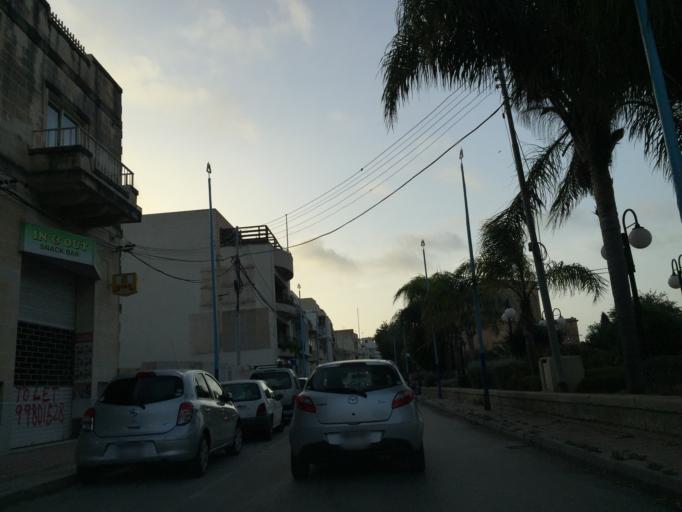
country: MT
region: Saint Paul's Bay
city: San Pawl il-Bahar
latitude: 35.9338
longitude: 14.4151
